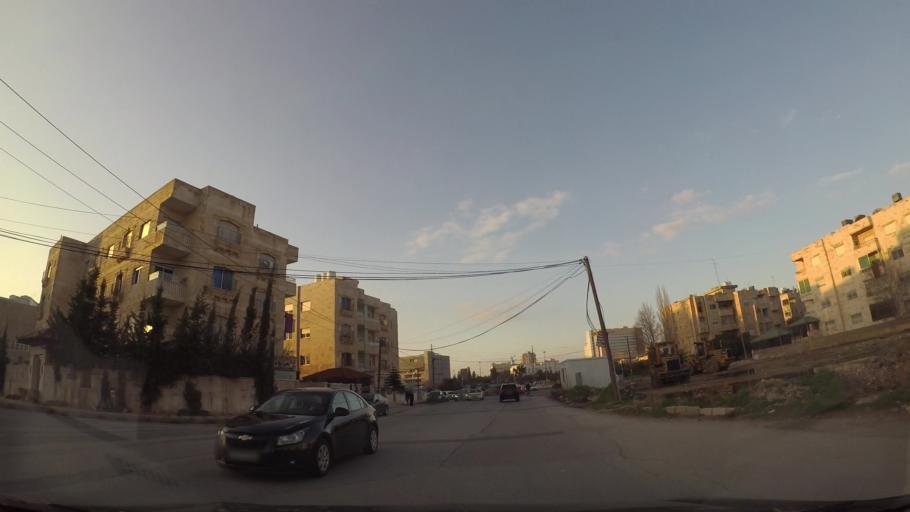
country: JO
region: Amman
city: Al Jubayhah
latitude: 31.9981
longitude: 35.8750
